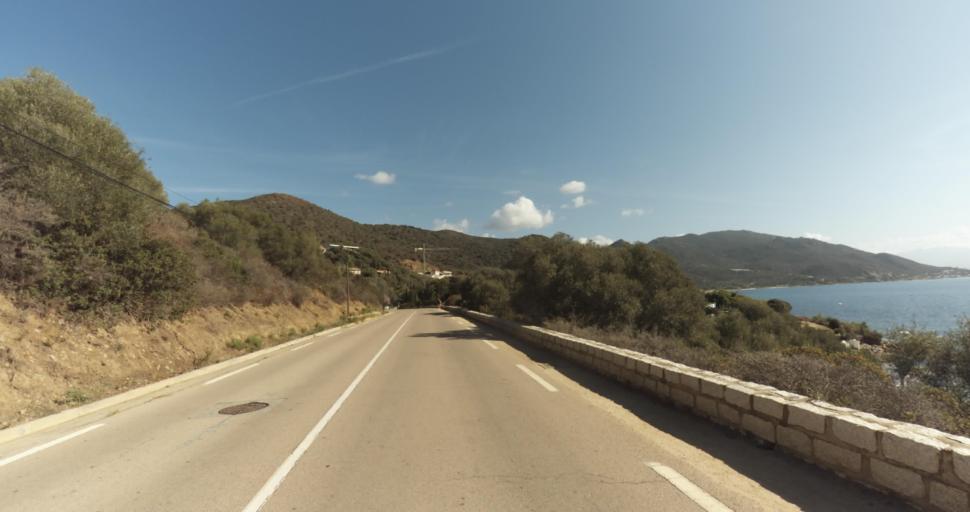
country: FR
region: Corsica
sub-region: Departement de la Corse-du-Sud
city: Ajaccio
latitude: 41.9042
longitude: 8.6262
